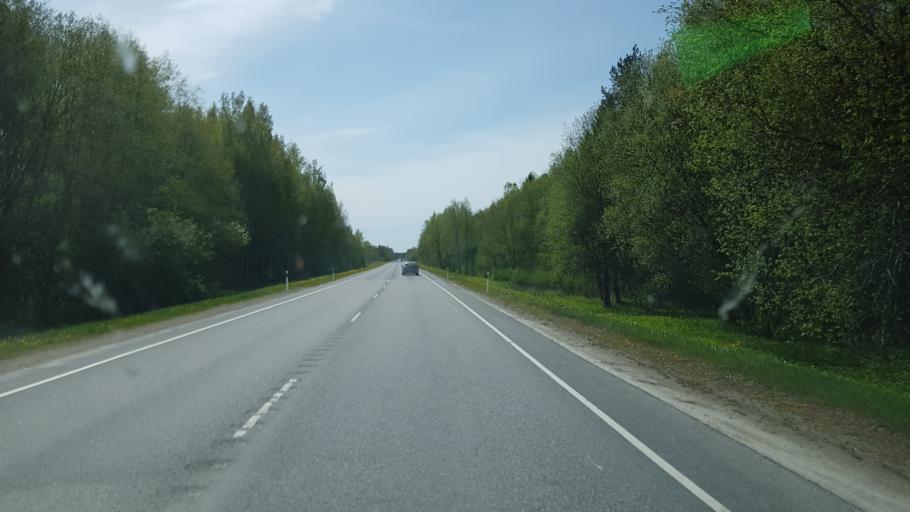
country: EE
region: Ida-Virumaa
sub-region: Johvi vald
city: Johvi
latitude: 59.1831
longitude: 27.3478
